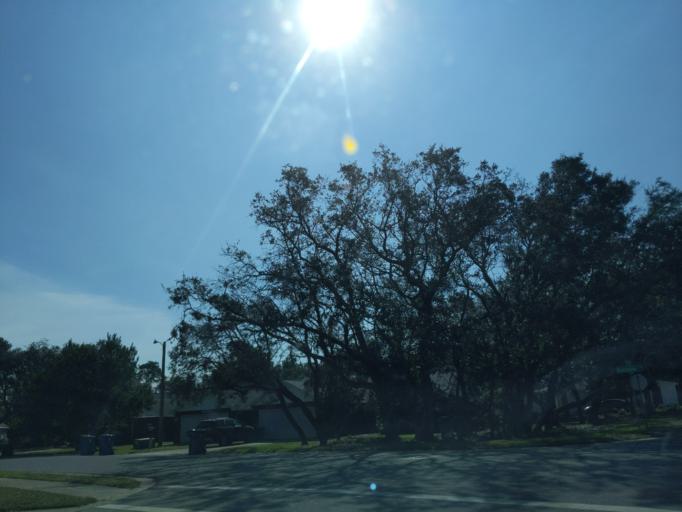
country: US
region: Florida
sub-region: Santa Rosa County
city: Gulf Breeze
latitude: 30.3620
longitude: -87.1724
